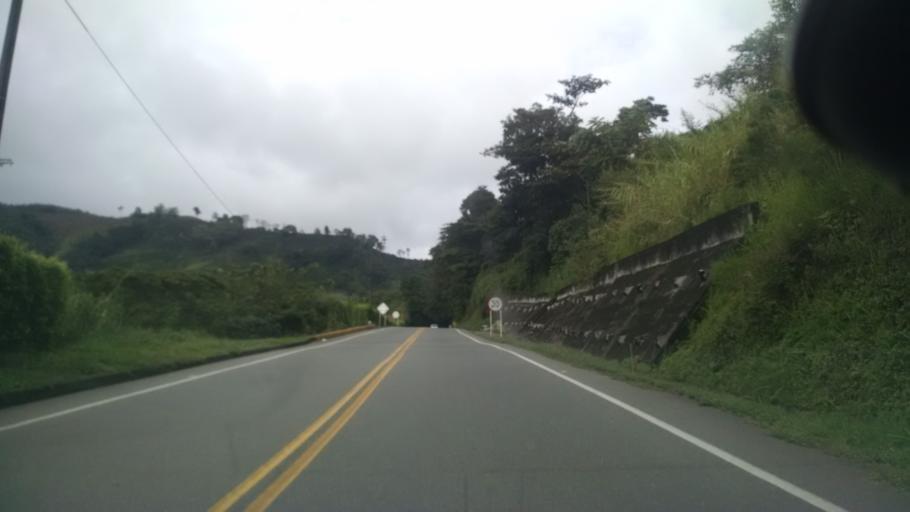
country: CO
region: Caldas
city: Palestina
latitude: 5.0639
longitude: -75.6156
